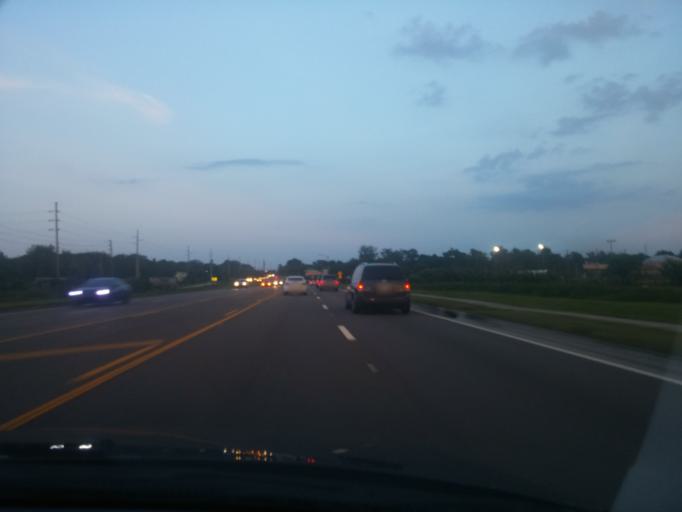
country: US
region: Florida
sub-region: Seminole County
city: Oviedo
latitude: 28.6553
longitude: -81.2179
